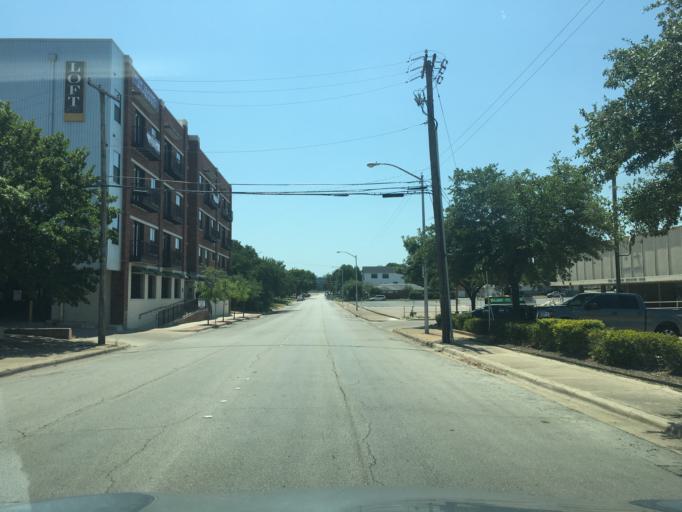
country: US
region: Texas
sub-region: Tarrant County
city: Fort Worth
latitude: 32.7057
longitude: -97.3535
